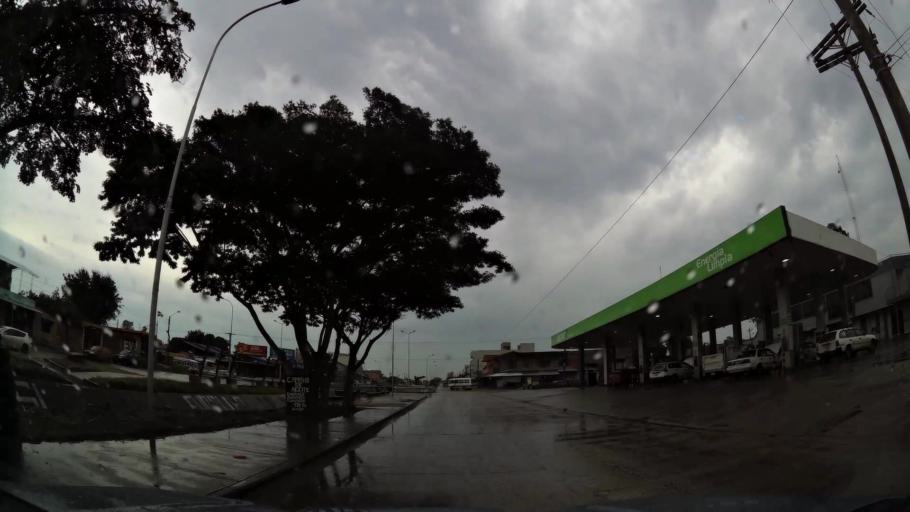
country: BO
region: Santa Cruz
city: Santa Cruz de la Sierra
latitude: -17.8119
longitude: -63.1365
